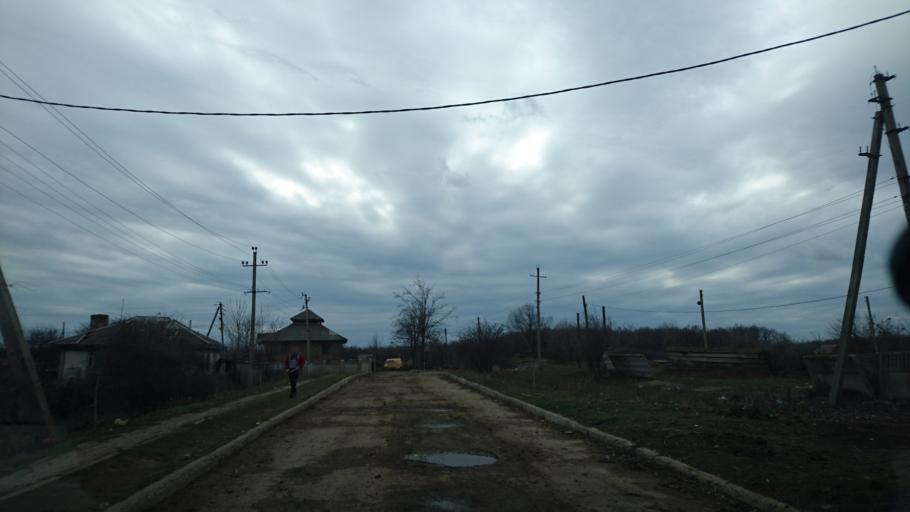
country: MD
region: Cantemir
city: Visniovca
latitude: 46.2897
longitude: 28.3735
